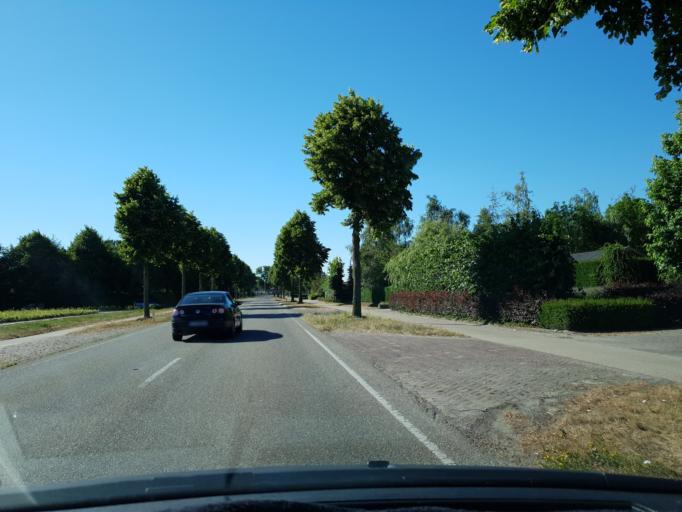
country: NL
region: North Brabant
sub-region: Gemeente Zundert
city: Zundert
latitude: 51.4673
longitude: 4.6863
